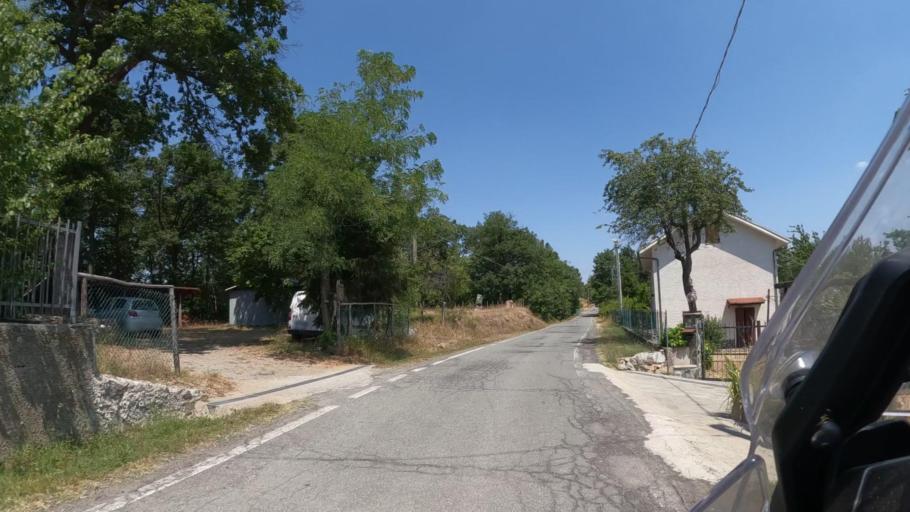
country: IT
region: Piedmont
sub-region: Provincia di Alessandria
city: Morbello
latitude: 44.5708
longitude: 8.5185
